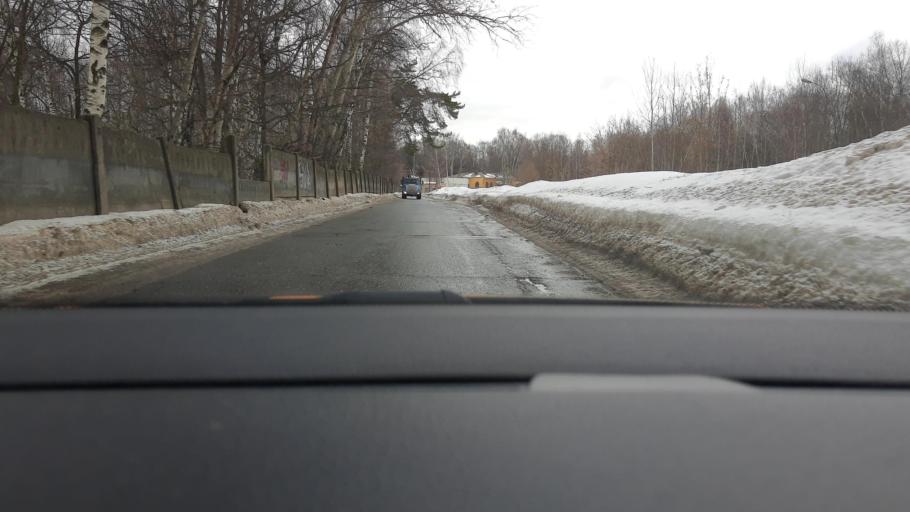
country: RU
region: Moscow
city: Babushkin
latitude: 55.8520
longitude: 37.7015
